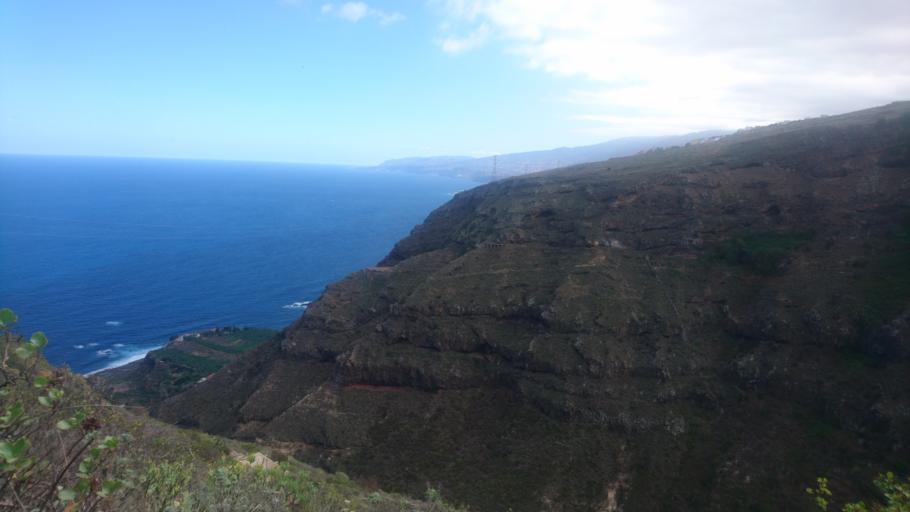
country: ES
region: Canary Islands
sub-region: Provincia de Santa Cruz de Tenerife
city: San Juan de la Rambla
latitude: 28.3862
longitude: -16.6296
